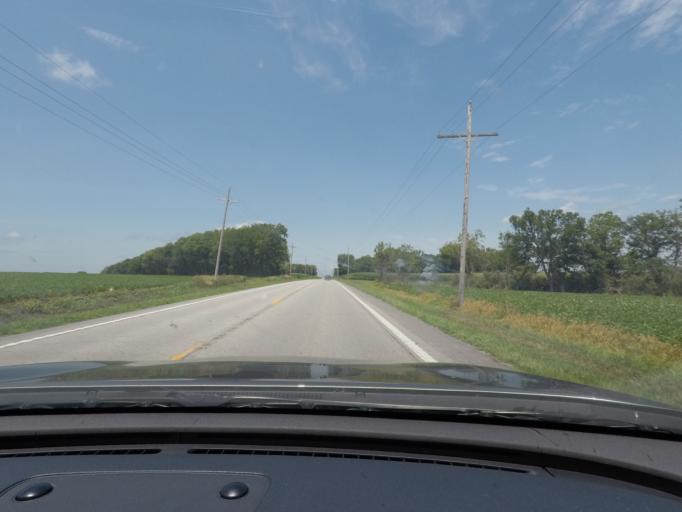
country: US
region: Missouri
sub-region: Saline County
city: Marshall
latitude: 39.1478
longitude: -93.2442
